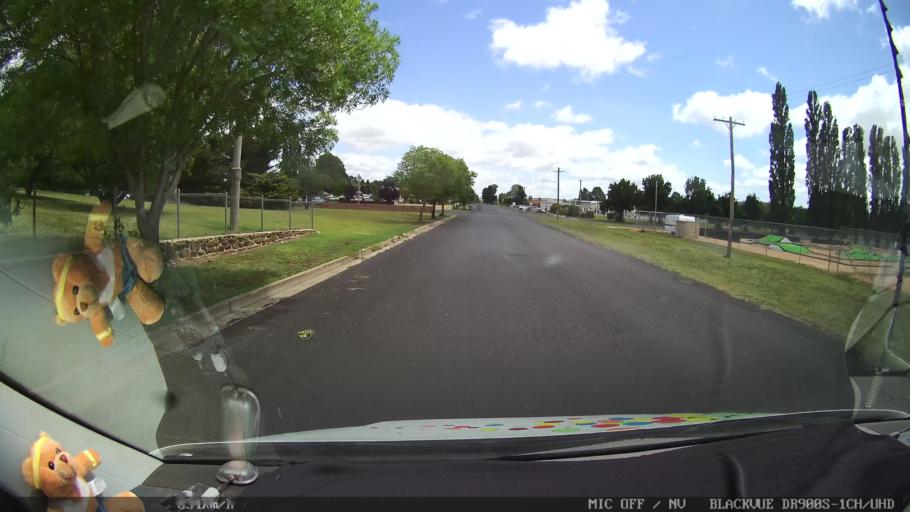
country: AU
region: New South Wales
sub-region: Glen Innes Severn
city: Glen Innes
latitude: -29.7339
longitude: 151.7330
